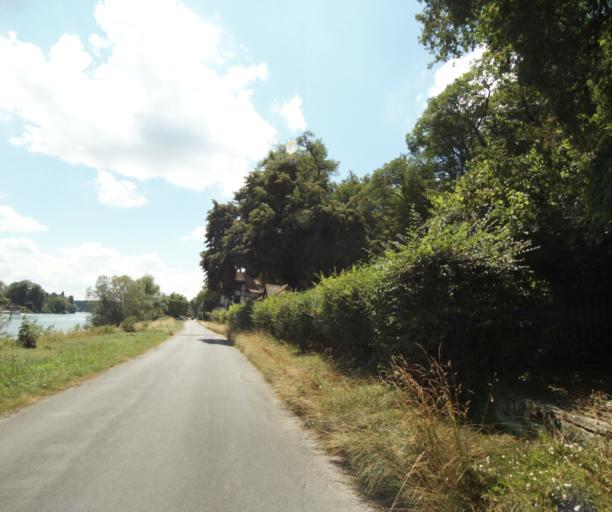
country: FR
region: Ile-de-France
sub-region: Departement de Seine-et-Marne
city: Samois-sur-Seine
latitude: 48.4397
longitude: 2.7463
